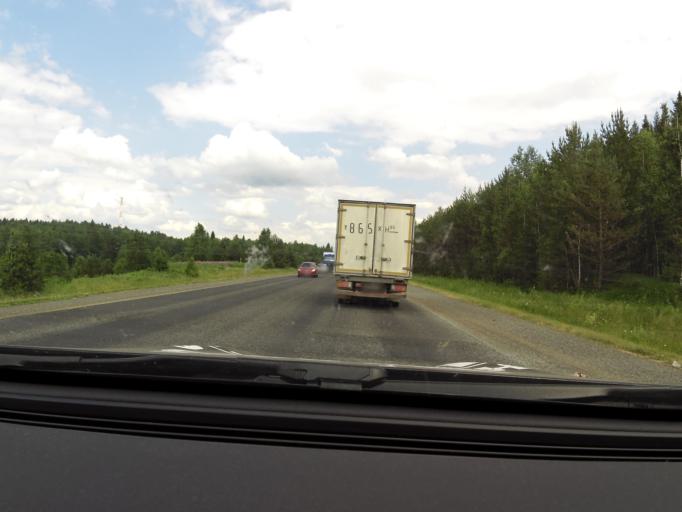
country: RU
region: Sverdlovsk
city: Arti
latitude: 56.7913
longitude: 58.4472
